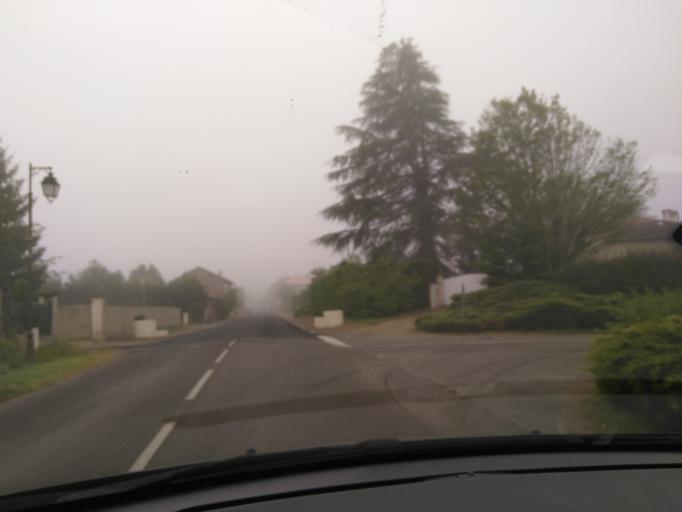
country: FR
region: Midi-Pyrenees
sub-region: Departement du Gers
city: Le Houga
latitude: 43.8569
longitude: -0.1801
